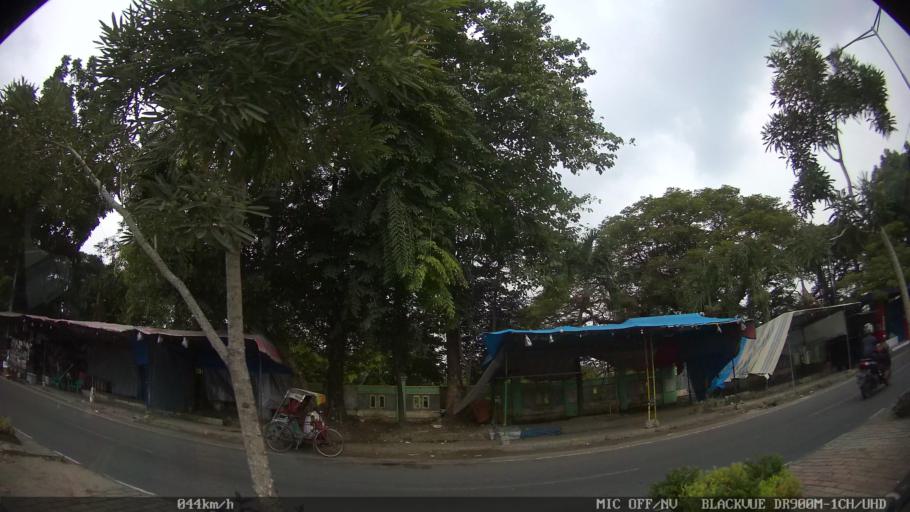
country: ID
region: North Sumatra
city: Medan
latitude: 3.5722
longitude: 98.6981
